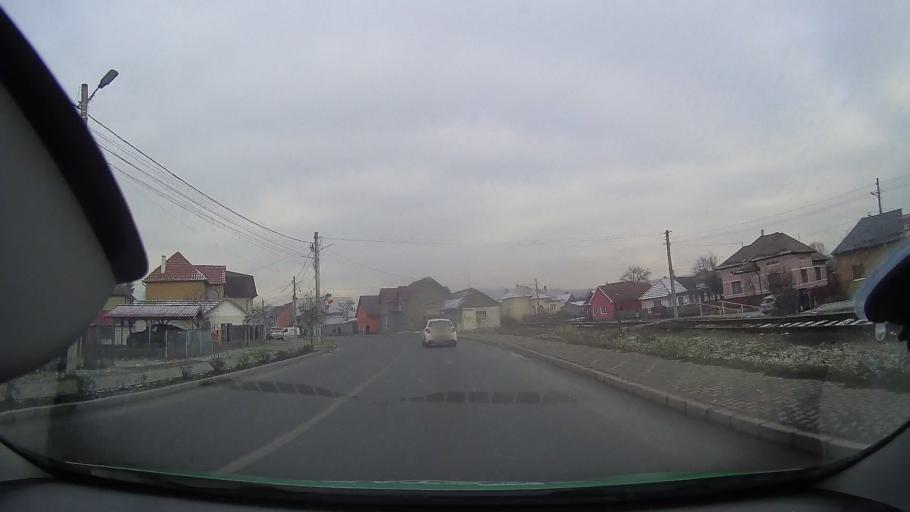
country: RO
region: Mures
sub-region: Comuna Ludus
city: Ludus
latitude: 46.4699
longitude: 24.0949
